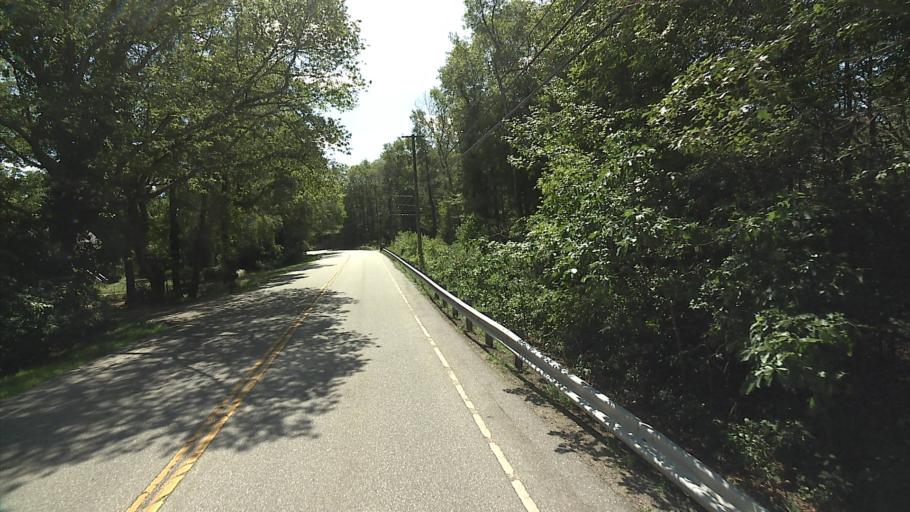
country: US
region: Rhode Island
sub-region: Washington County
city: Hopkinton
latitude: 41.5595
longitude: -71.8132
